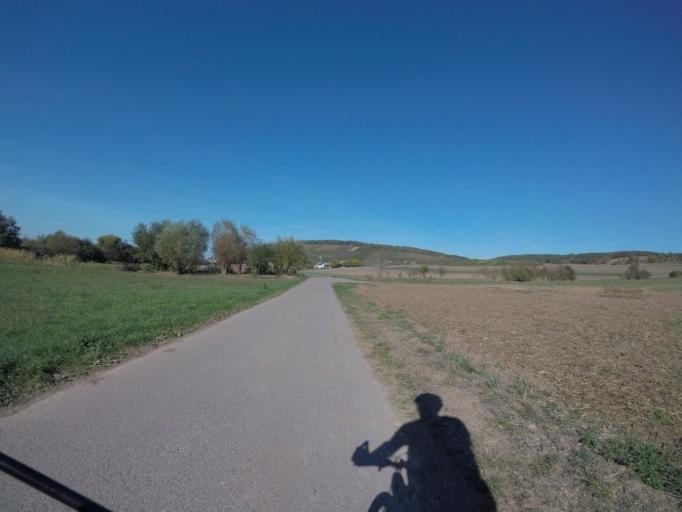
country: DE
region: Baden-Wuerttemberg
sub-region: Karlsruhe Region
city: Illingen
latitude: 48.9911
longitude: 8.9579
